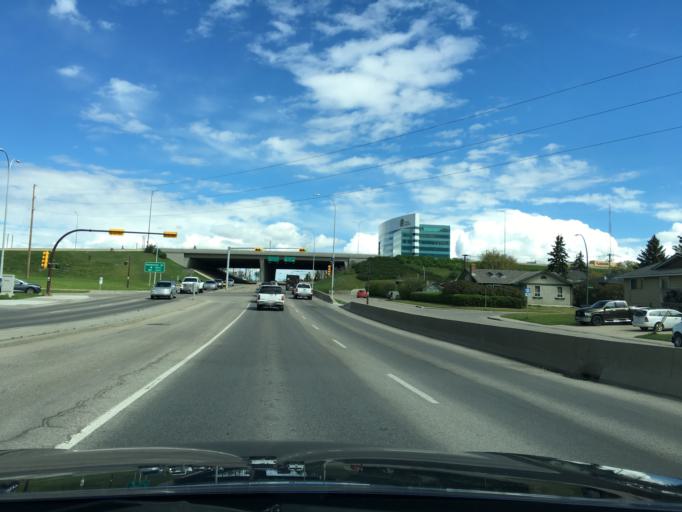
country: CA
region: Alberta
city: Calgary
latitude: 51.0431
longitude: -114.0019
